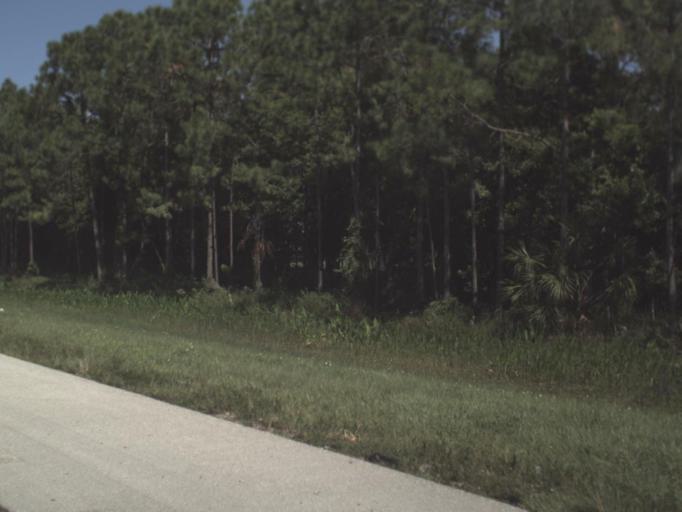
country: US
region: Florida
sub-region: Lee County
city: Bonita Springs
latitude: 26.2919
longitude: -81.7427
